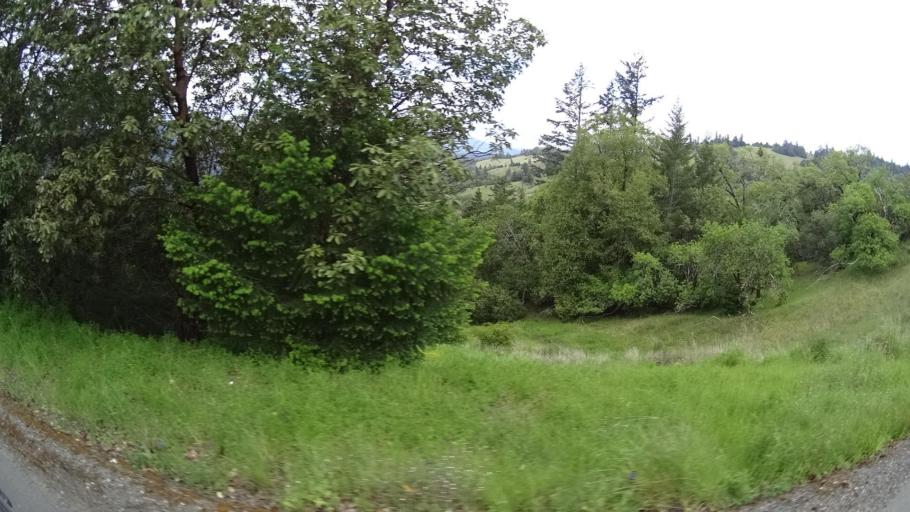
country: US
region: California
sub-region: Humboldt County
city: Redway
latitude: 40.1124
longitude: -123.7754
